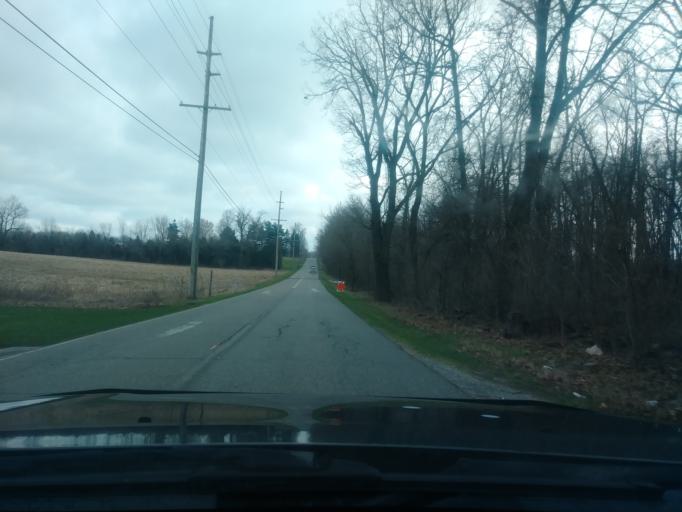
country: US
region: Indiana
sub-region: LaPorte County
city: LaPorte
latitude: 41.6248
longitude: -86.7965
